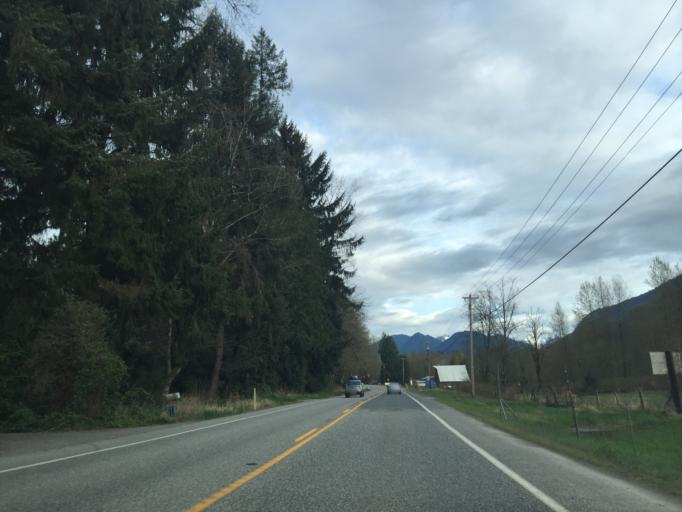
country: US
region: Washington
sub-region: Snohomish County
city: Arlington Heights
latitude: 48.2703
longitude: -121.9413
